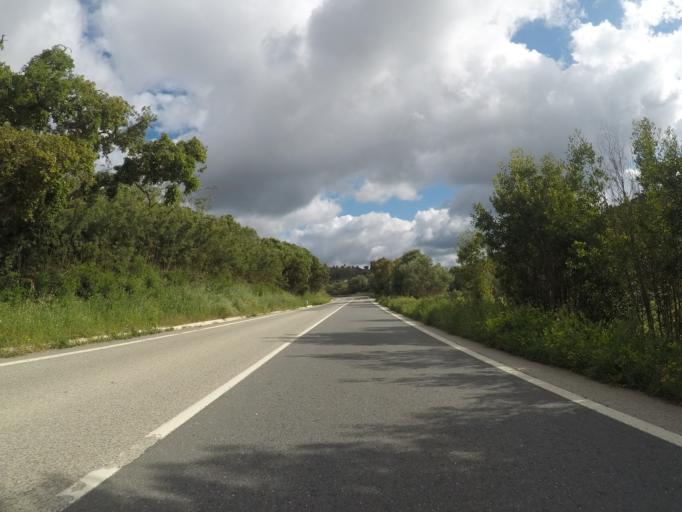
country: PT
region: Faro
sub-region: Lagos
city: Lagos
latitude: 37.1602
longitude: -8.7430
